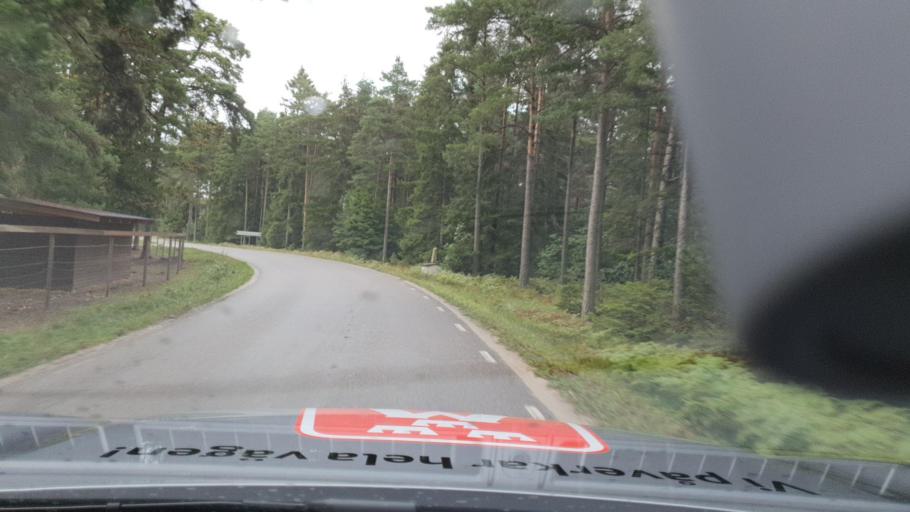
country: SE
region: Gotland
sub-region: Gotland
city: Vibble
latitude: 57.5162
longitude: 18.2173
